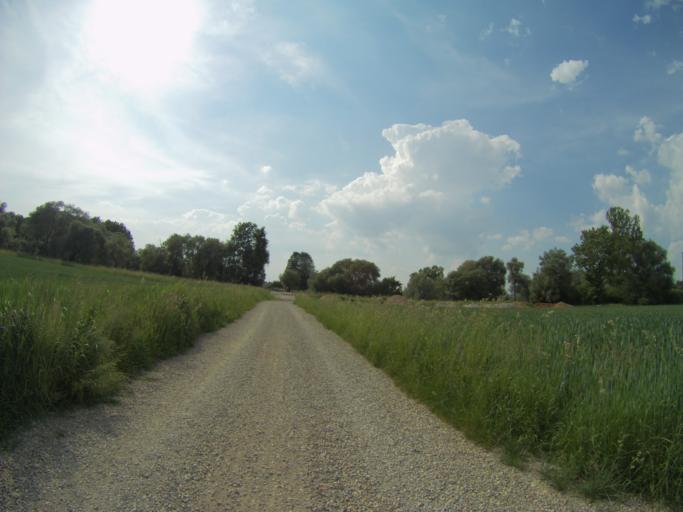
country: DE
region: Bavaria
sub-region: Upper Bavaria
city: Haag an der Amper
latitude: 48.4415
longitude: 11.8006
